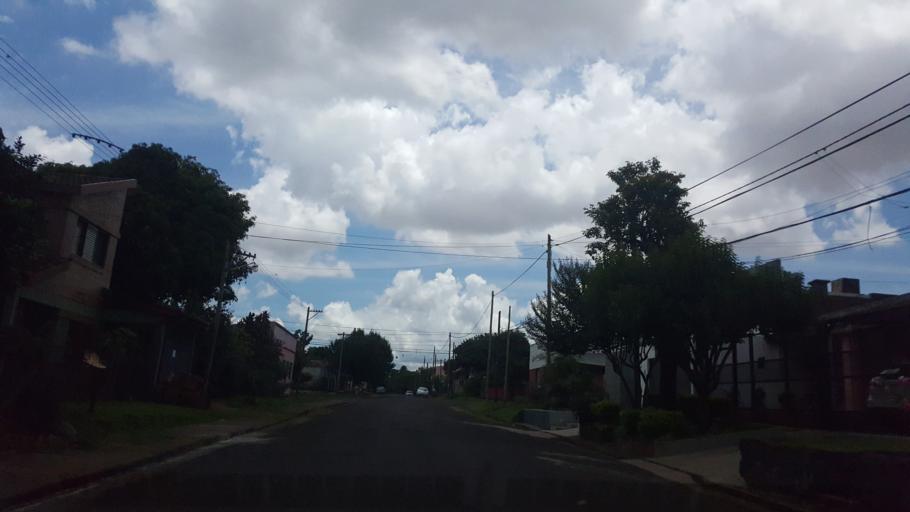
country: AR
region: Misiones
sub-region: Departamento de Capital
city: Posadas
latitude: -27.3714
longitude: -55.9139
